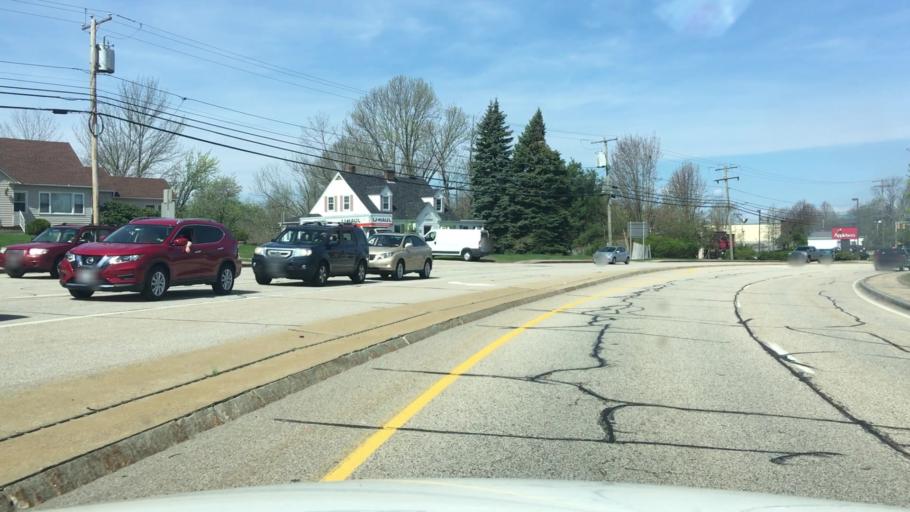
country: US
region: Maine
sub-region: York County
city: South Eliot
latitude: 43.0866
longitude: -70.7881
